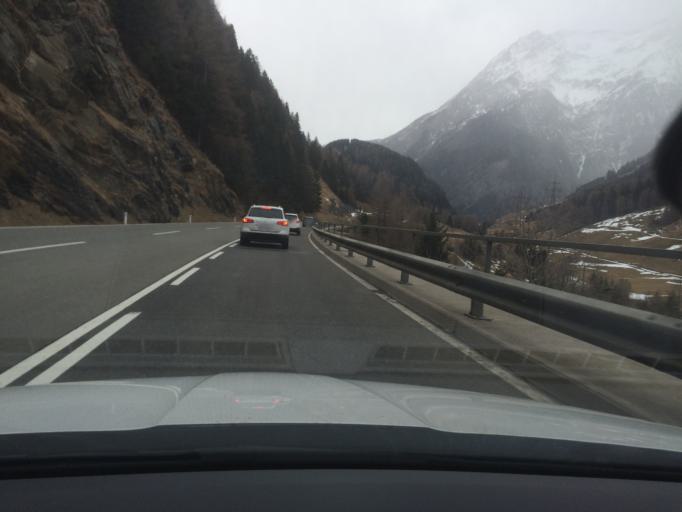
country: AT
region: Tyrol
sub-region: Politischer Bezirk Lienz
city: Matrei in Osttirol
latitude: 47.0680
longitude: 12.5319
